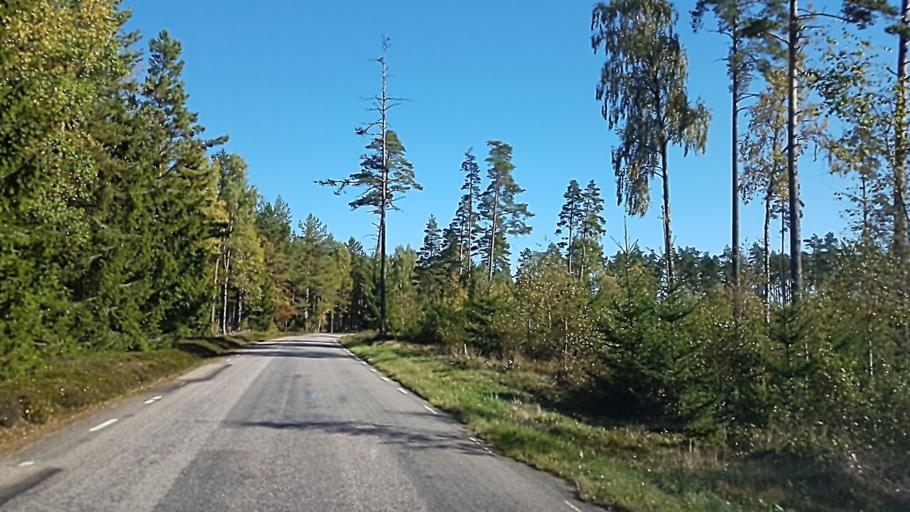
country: SE
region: Kronoberg
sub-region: Ljungby Kommun
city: Ljungby
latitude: 56.8172
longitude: 14.0404
